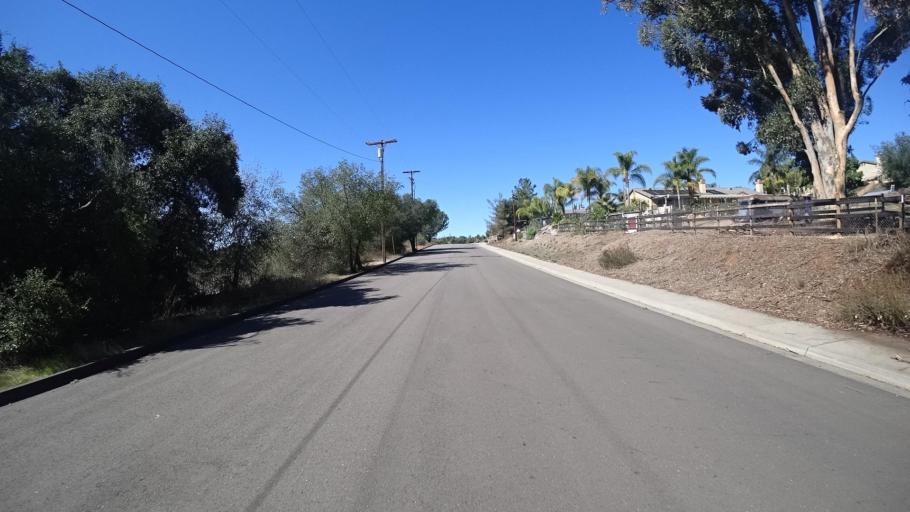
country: US
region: California
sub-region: San Diego County
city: Alpine
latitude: 32.8377
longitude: -116.7415
